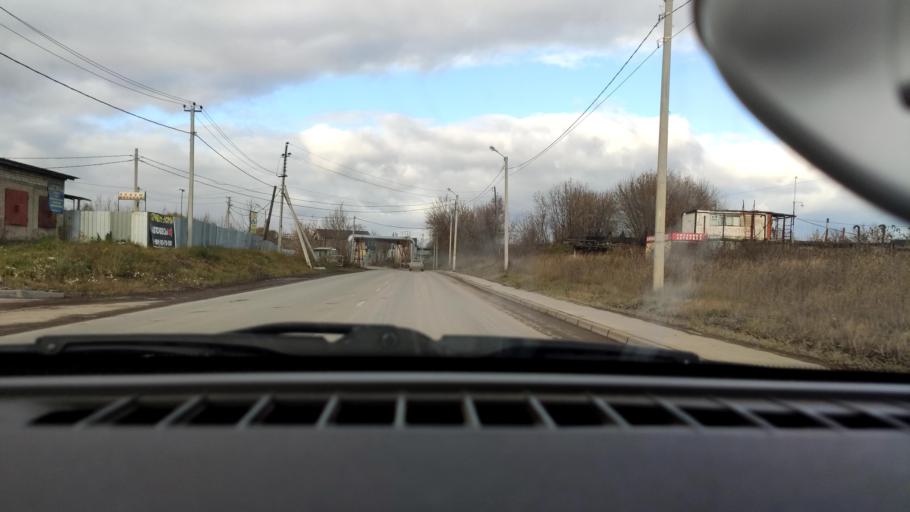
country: RU
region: Perm
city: Kondratovo
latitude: 57.9511
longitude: 56.1382
